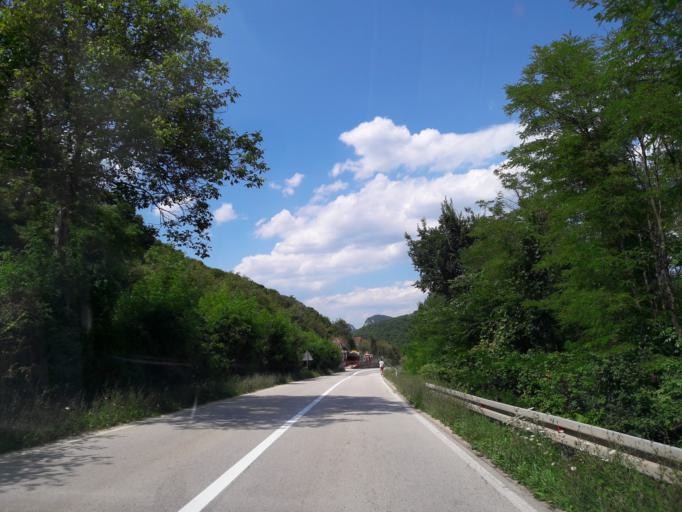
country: BA
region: Republika Srpska
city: Mrkonjic Grad
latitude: 44.5343
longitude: 17.1499
